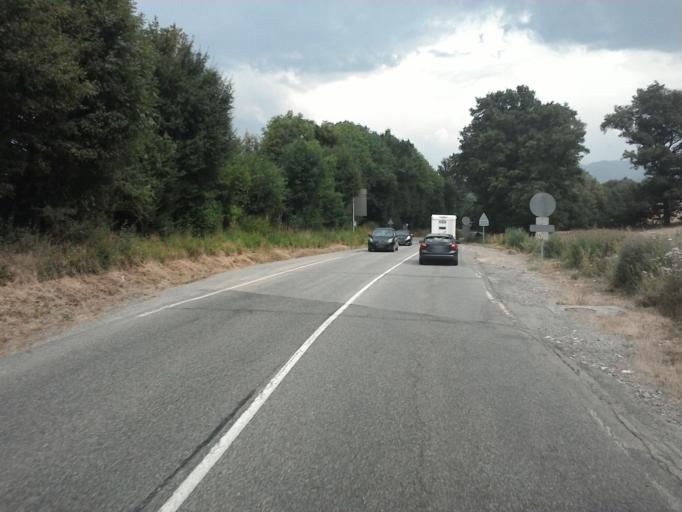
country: FR
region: Rhone-Alpes
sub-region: Departement de l'Isere
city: La Mure
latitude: 44.9014
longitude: 5.7996
